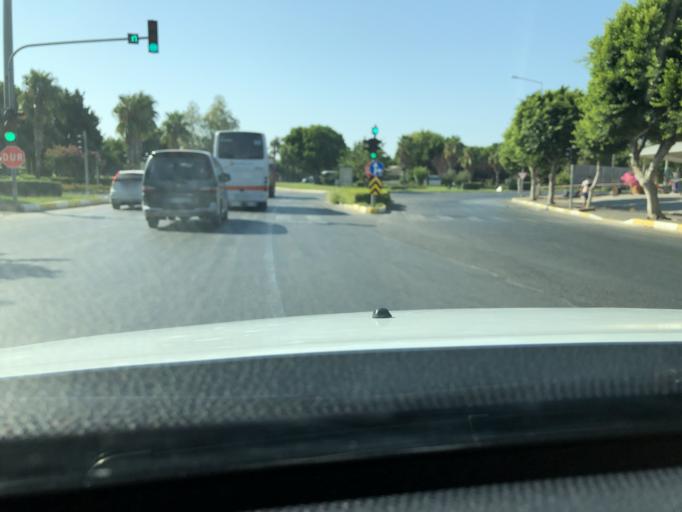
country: TR
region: Antalya
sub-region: Manavgat
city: Side
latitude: 36.7770
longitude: 31.3969
